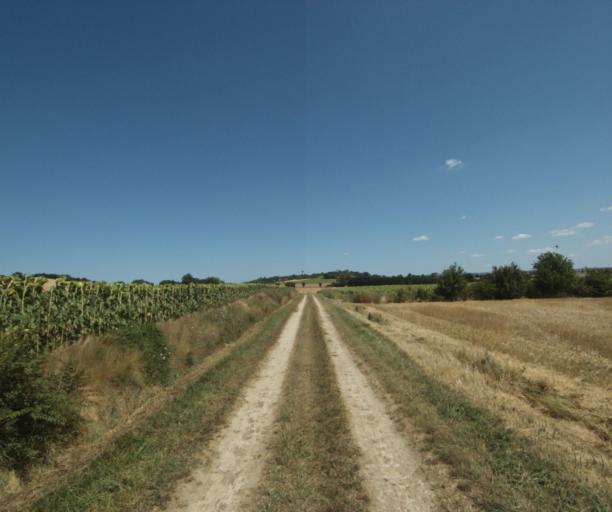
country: FR
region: Midi-Pyrenees
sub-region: Departement de la Haute-Garonne
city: Saint-Felix-Lauragais
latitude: 43.4946
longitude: 1.8778
